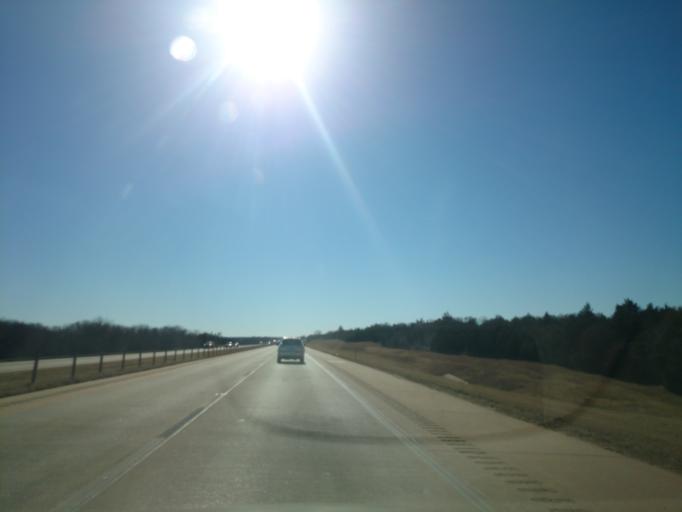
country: US
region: Oklahoma
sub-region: Oklahoma County
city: Edmond
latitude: 35.7533
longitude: -97.4164
